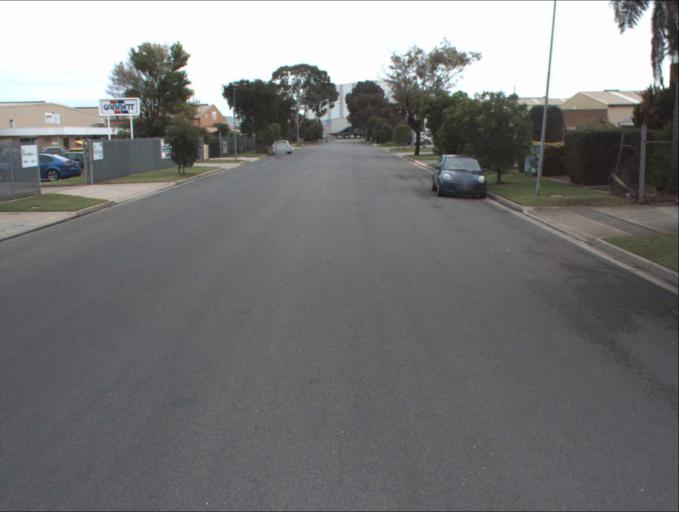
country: AU
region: South Australia
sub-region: Port Adelaide Enfield
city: Blair Athol
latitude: -34.8569
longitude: 138.5736
